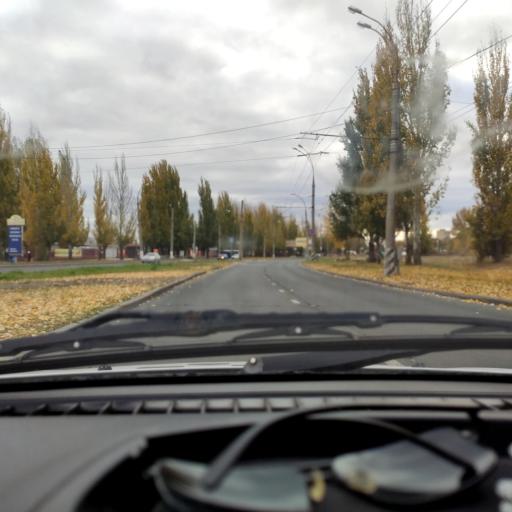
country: RU
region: Samara
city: Tol'yatti
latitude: 53.5428
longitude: 49.2790
